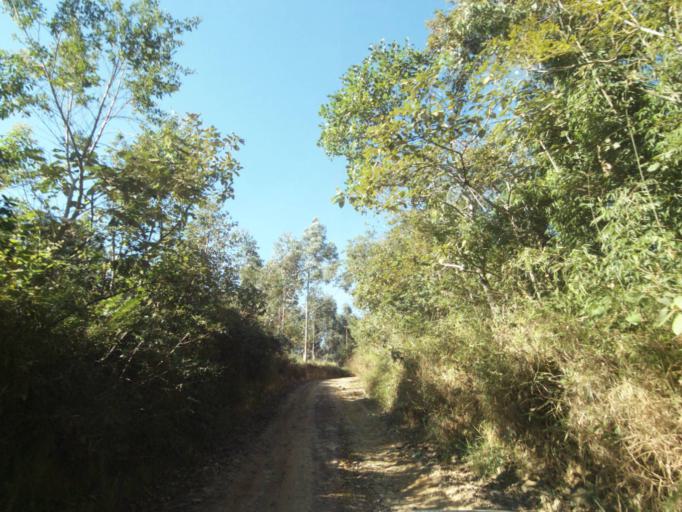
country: BR
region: Parana
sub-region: Tibagi
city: Tibagi
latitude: -24.5727
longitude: -50.4750
